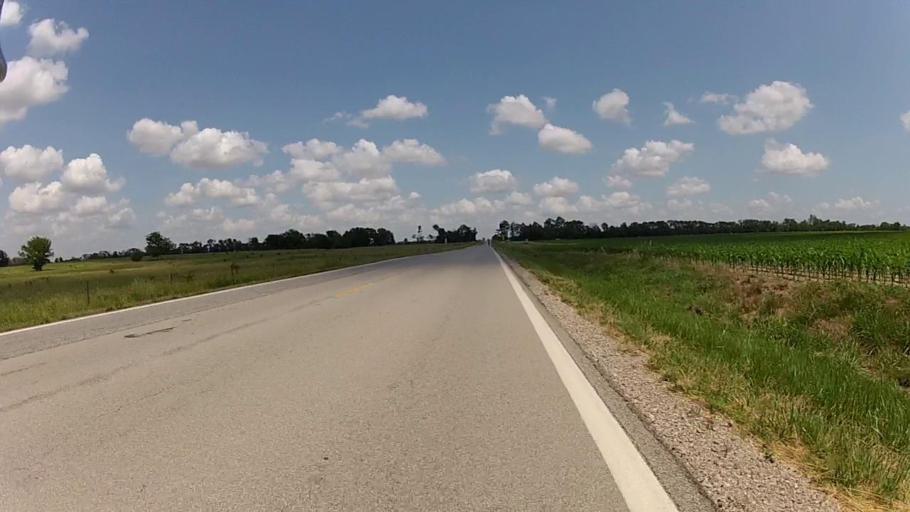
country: US
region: Kansas
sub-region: Labette County
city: Altamont
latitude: 37.1926
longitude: -95.3715
